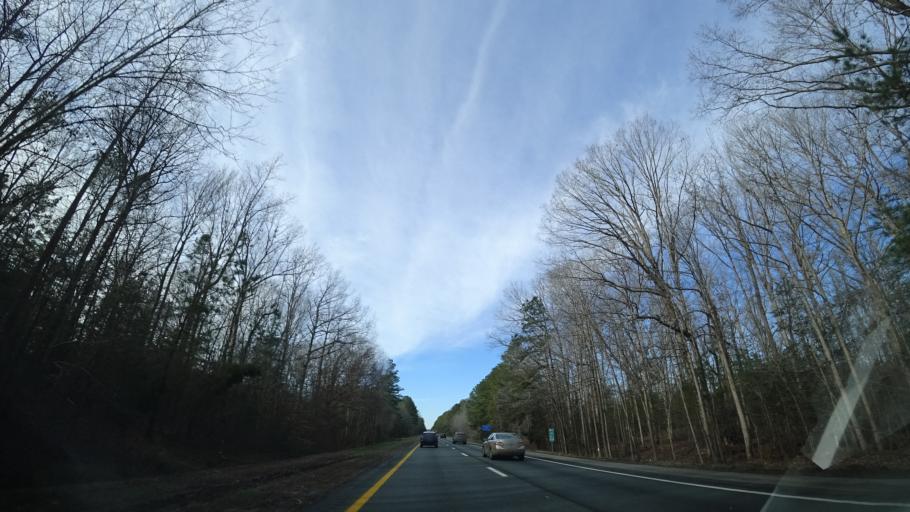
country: US
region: Virginia
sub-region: New Kent County
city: New Kent
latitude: 37.4823
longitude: -76.9428
